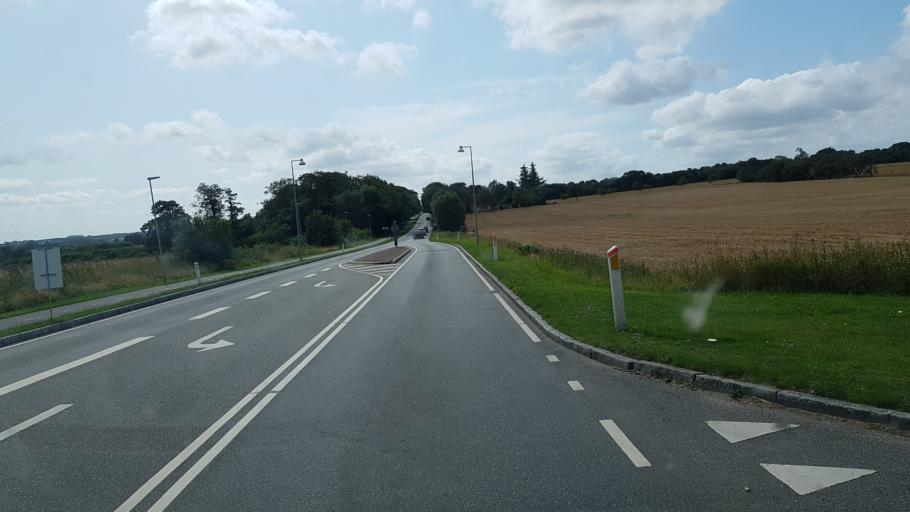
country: DK
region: South Denmark
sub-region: Vejen Kommune
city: Vejen
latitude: 55.5658
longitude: 9.1335
